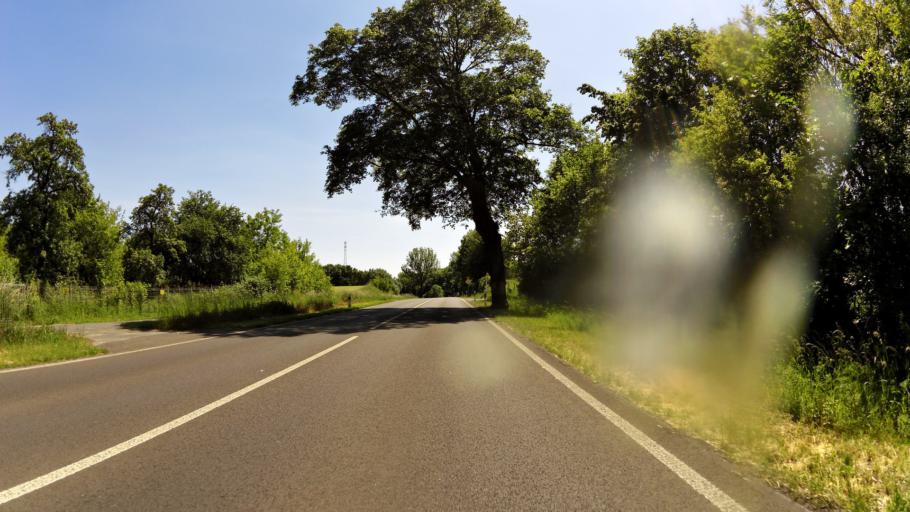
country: DE
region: Brandenburg
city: Frankfurt (Oder)
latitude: 52.3725
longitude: 14.5227
